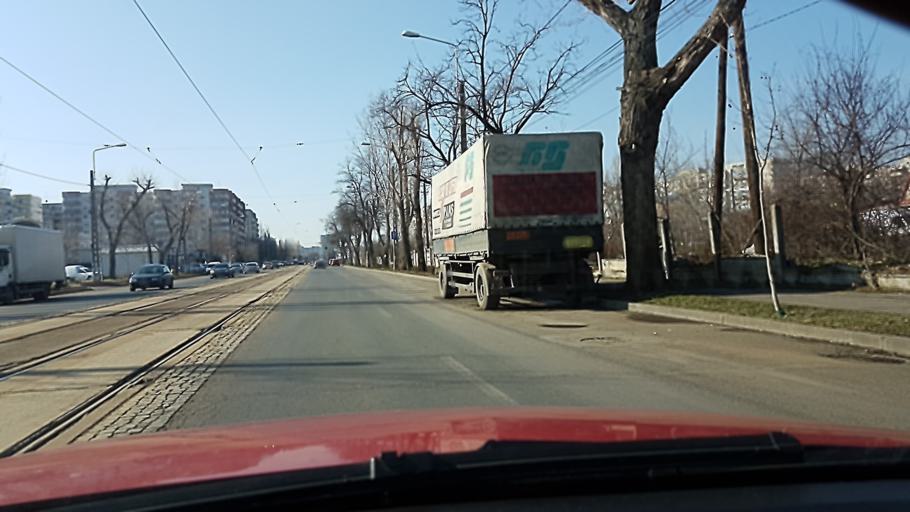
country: RO
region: Ilfov
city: Dobroesti
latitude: 44.4357
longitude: 26.1759
